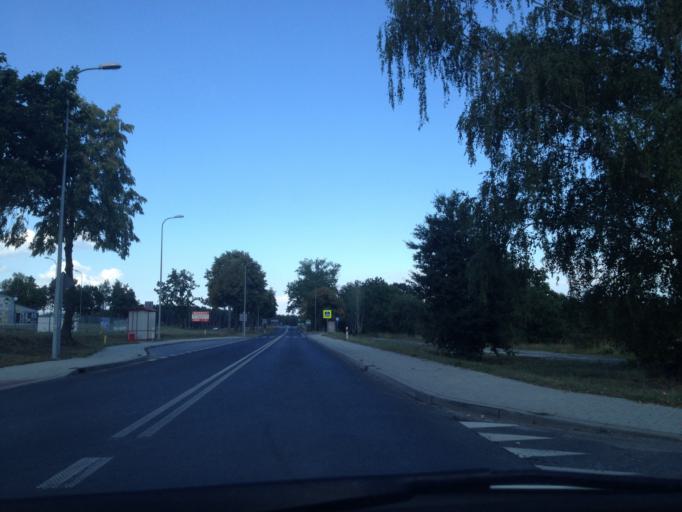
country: PL
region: Lubusz
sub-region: Powiat zaganski
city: Ilowa
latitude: 51.5212
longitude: 15.2154
